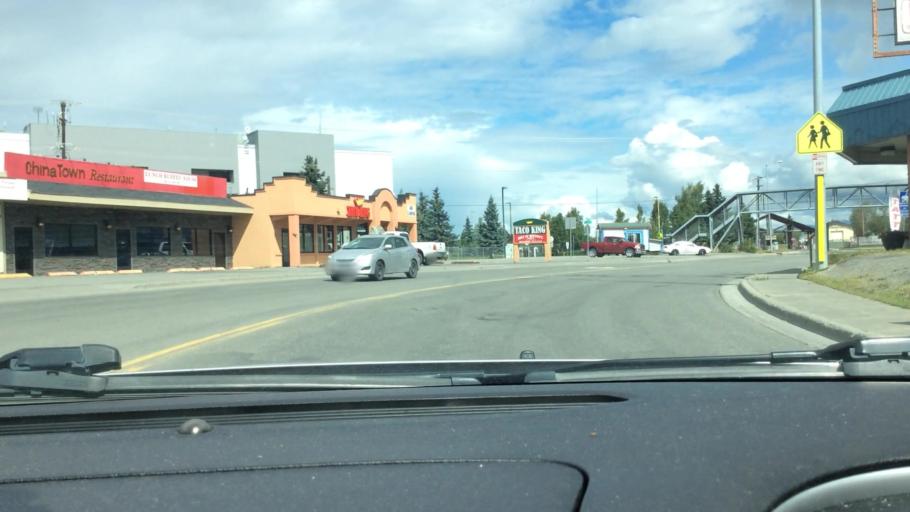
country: US
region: Alaska
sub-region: Anchorage Municipality
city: Anchorage
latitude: 61.2306
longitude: -149.8742
